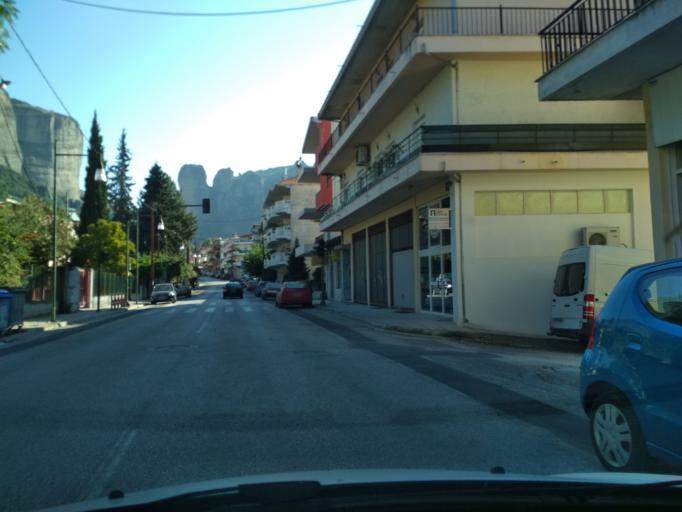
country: GR
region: Thessaly
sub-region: Trikala
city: Kalampaka
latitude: 39.7054
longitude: 21.6194
